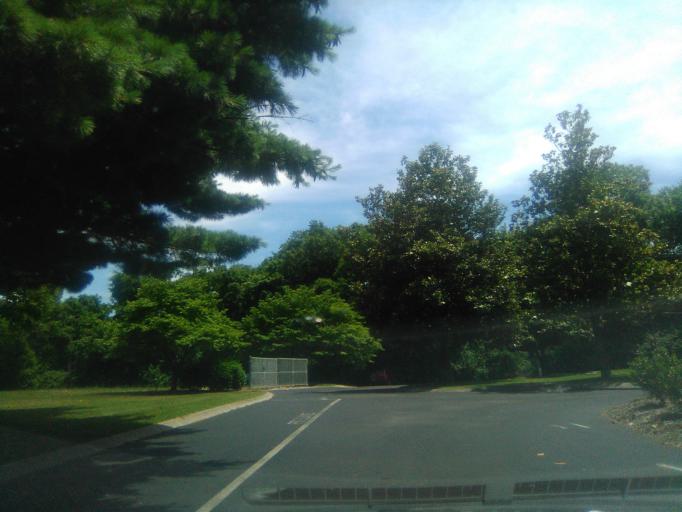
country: US
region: Tennessee
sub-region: Davidson County
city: Belle Meade
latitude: 36.1281
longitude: -86.8508
